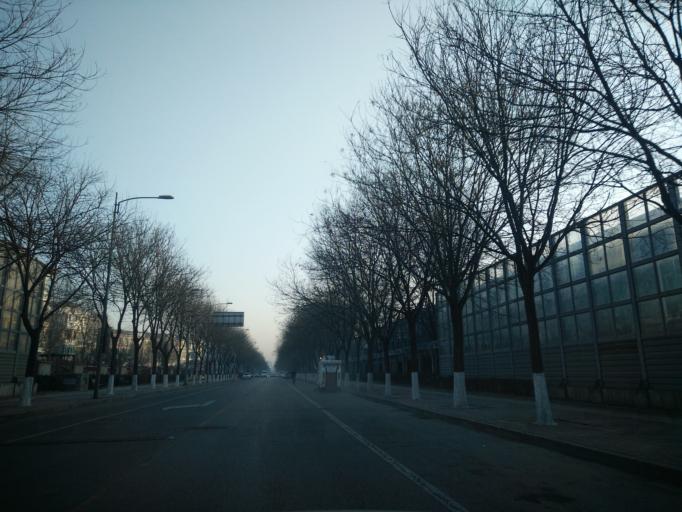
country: CN
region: Beijing
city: Jiugong
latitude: 39.7867
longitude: 116.4844
